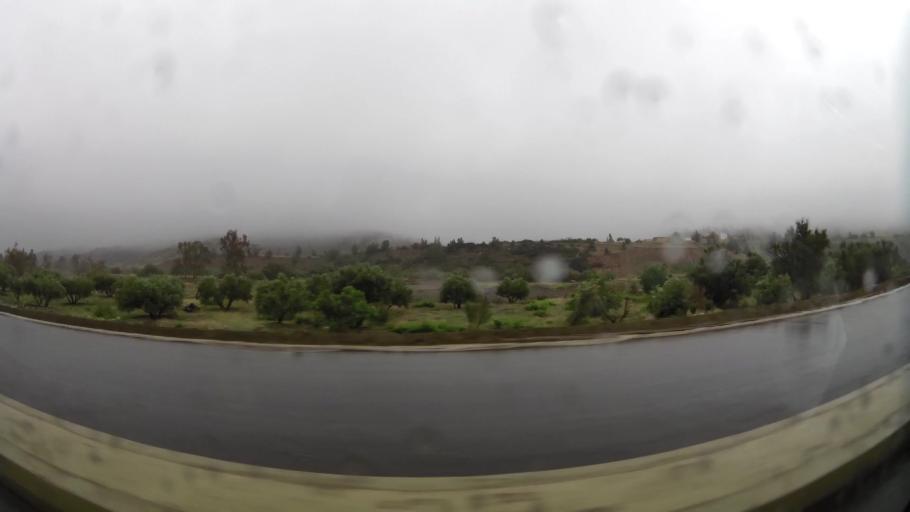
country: MA
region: Taza-Al Hoceima-Taounate
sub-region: Taza
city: Aknoul
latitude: 34.7957
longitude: -3.7459
